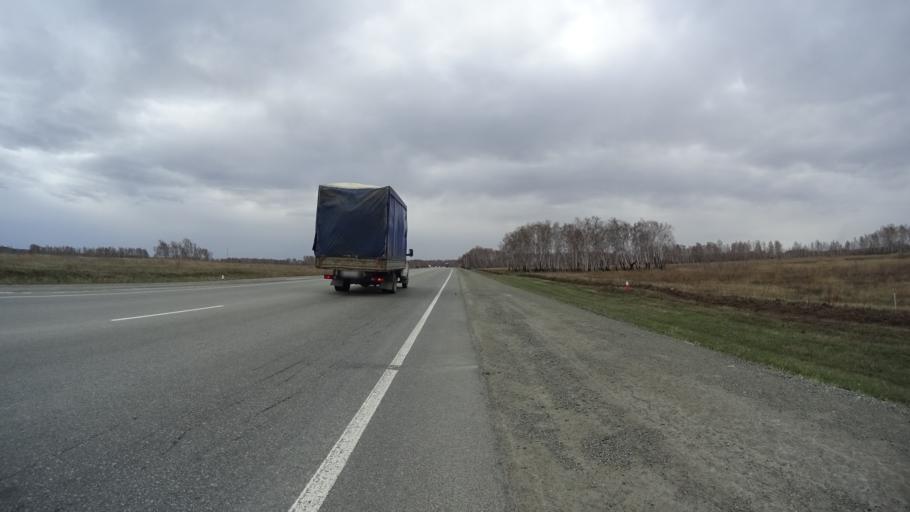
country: RU
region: Chelyabinsk
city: Yemanzhelinsk
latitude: 54.7010
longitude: 61.2529
